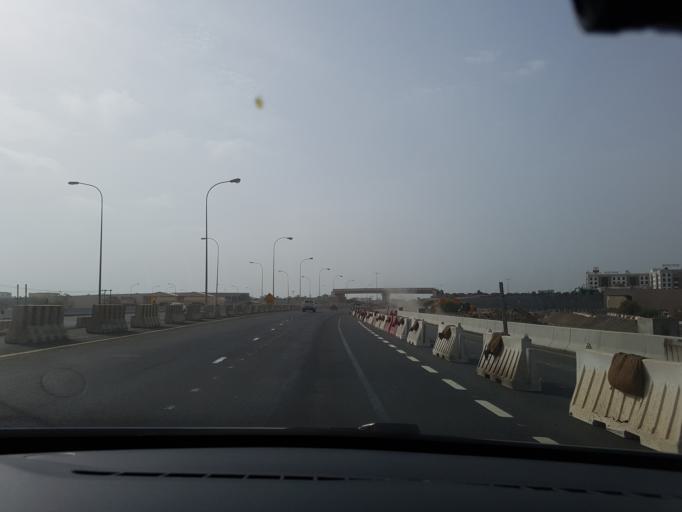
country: OM
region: Al Batinah
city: Al Sohar
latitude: 24.3883
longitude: 56.6990
